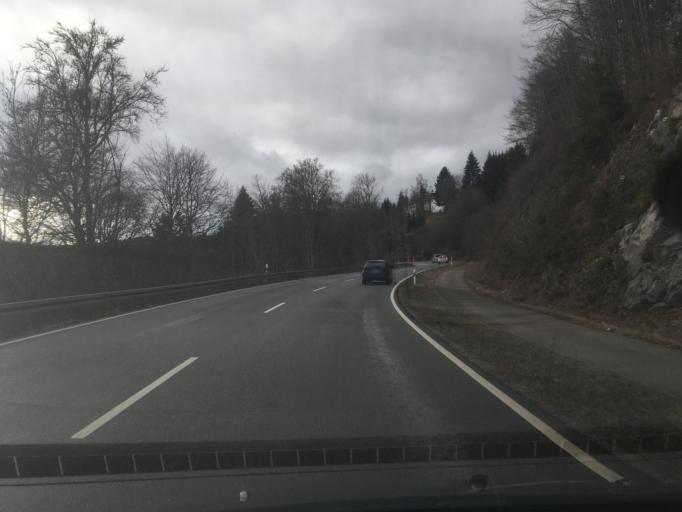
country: DE
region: Baden-Wuerttemberg
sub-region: Freiburg Region
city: Hausern
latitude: 47.7570
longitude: 8.1840
